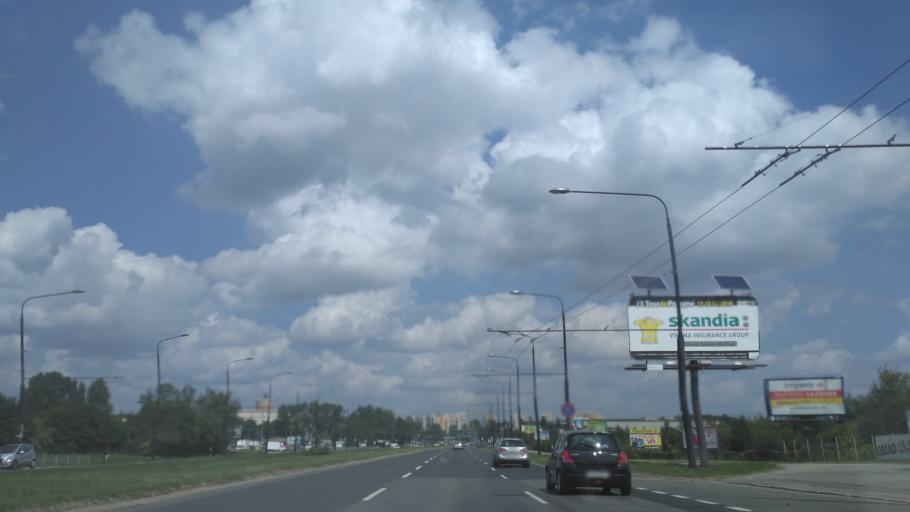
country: PL
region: Lublin Voivodeship
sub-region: Powiat lubelski
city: Lublin
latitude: 51.2435
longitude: 22.5734
